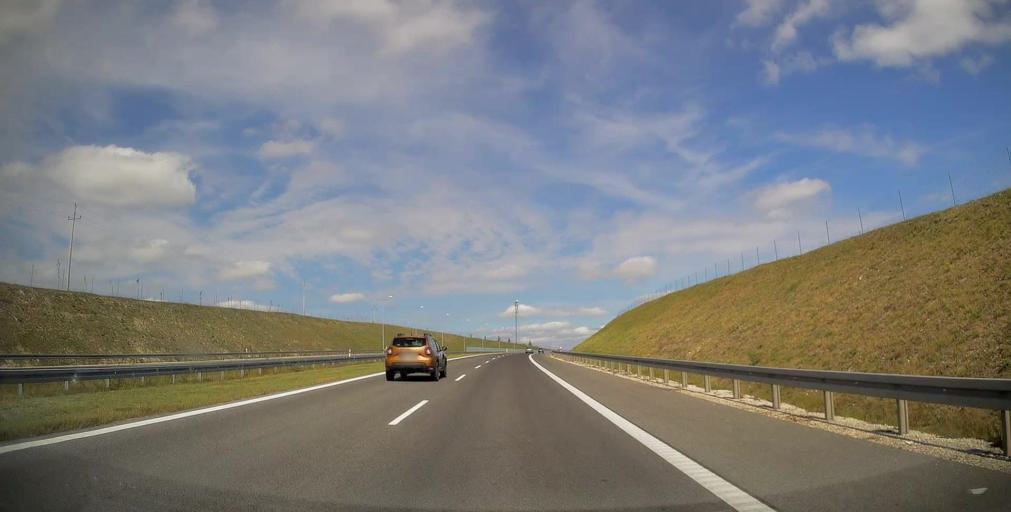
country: PL
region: Swietokrzyskie
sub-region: Powiat jedrzejowski
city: Wodzislaw
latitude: 50.5531
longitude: 20.2018
